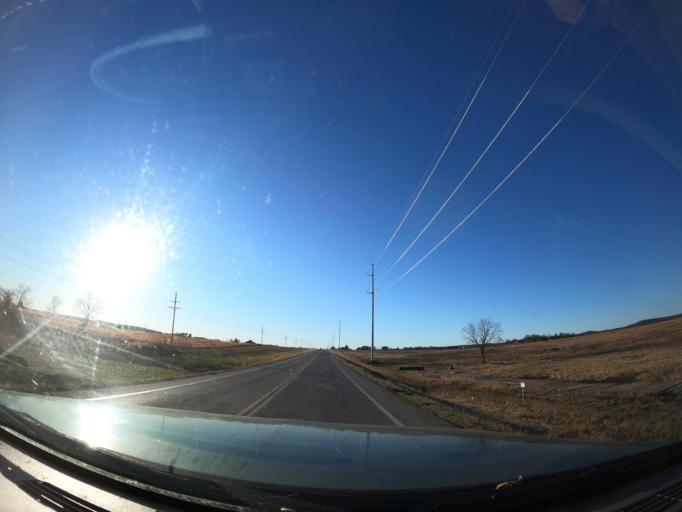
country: US
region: Oklahoma
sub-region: Latimer County
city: Wilburton
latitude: 34.9129
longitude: -95.4082
